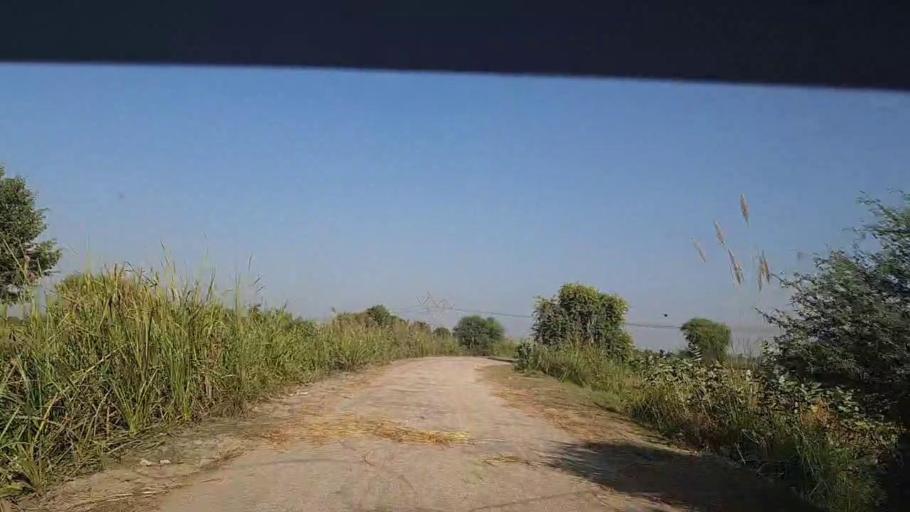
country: PK
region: Sindh
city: Larkana
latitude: 27.6217
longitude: 68.2475
